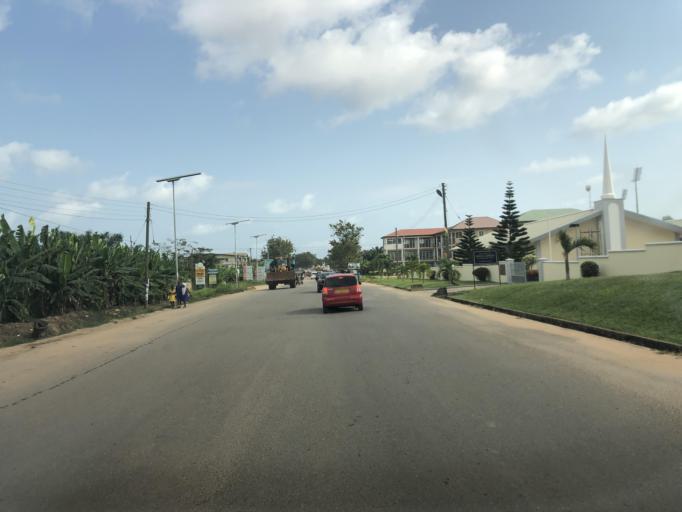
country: GH
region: Central
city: Cape Coast
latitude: 5.1409
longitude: -1.2825
